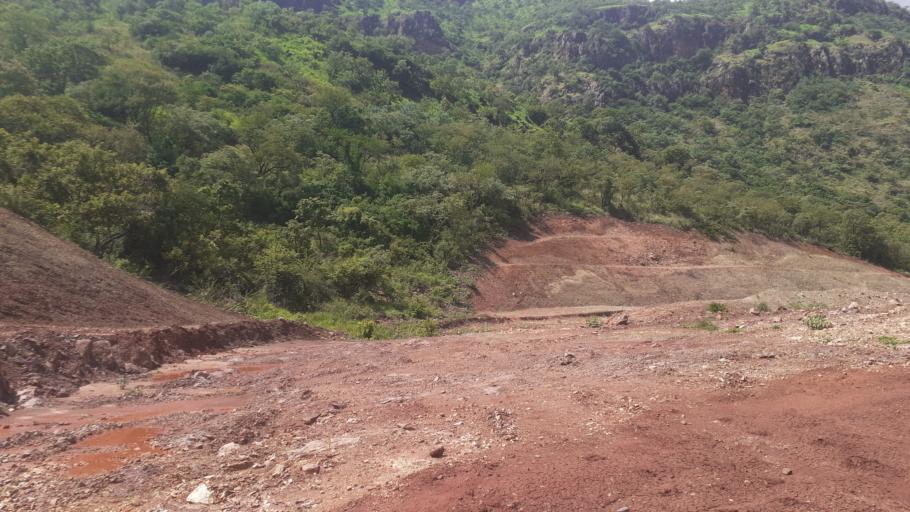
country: ET
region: Southern Nations, Nationalities, and People's Region
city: Areka
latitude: 7.6131
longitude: 37.5134
